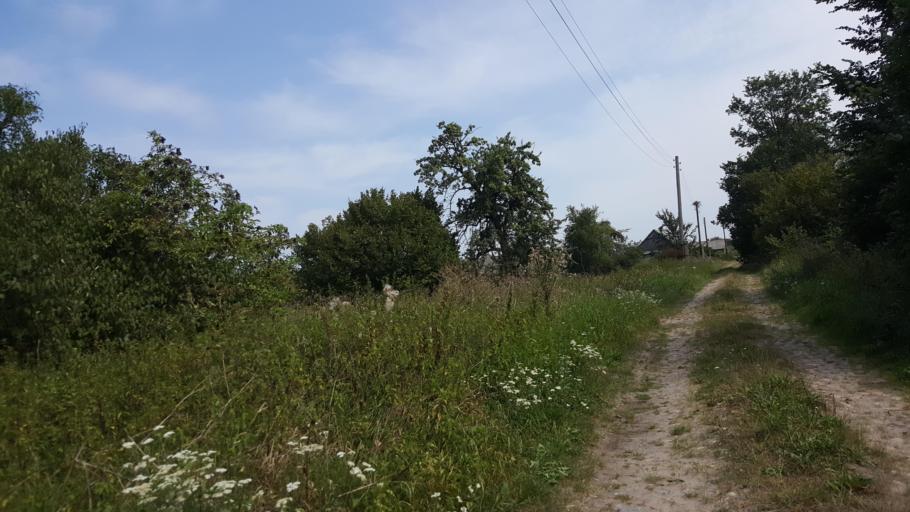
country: BY
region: Brest
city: Kamyanyets
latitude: 52.4518
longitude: 23.6493
